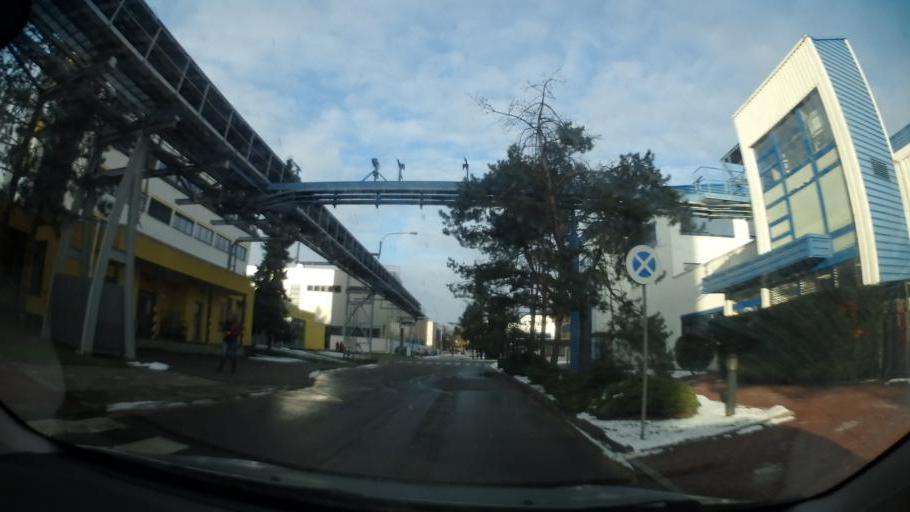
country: CZ
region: South Moravian
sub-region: Mesto Brno
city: Mokra Hora
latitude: 49.2510
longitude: 16.5927
